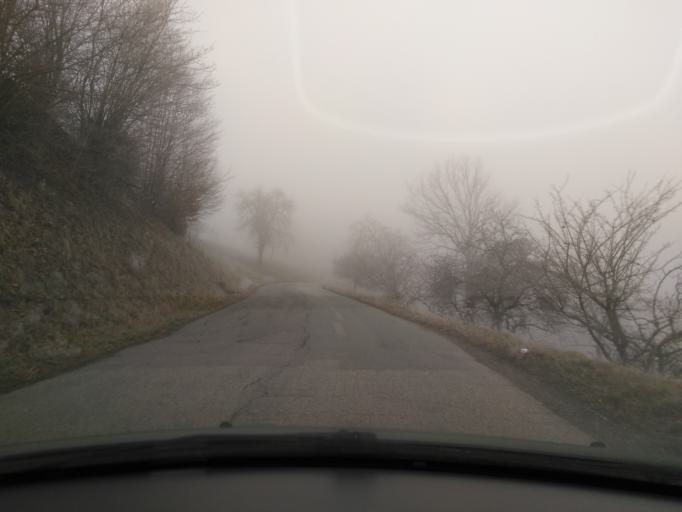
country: FR
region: Rhone-Alpes
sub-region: Departement de la Haute-Savoie
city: Sallanches
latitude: 45.9374
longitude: 6.6232
